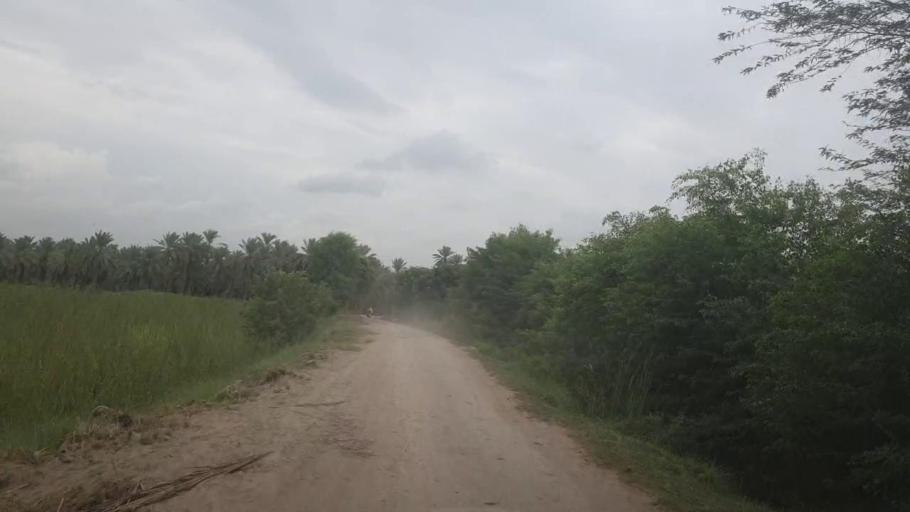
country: PK
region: Sindh
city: Khairpur
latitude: 27.5824
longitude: 68.7117
